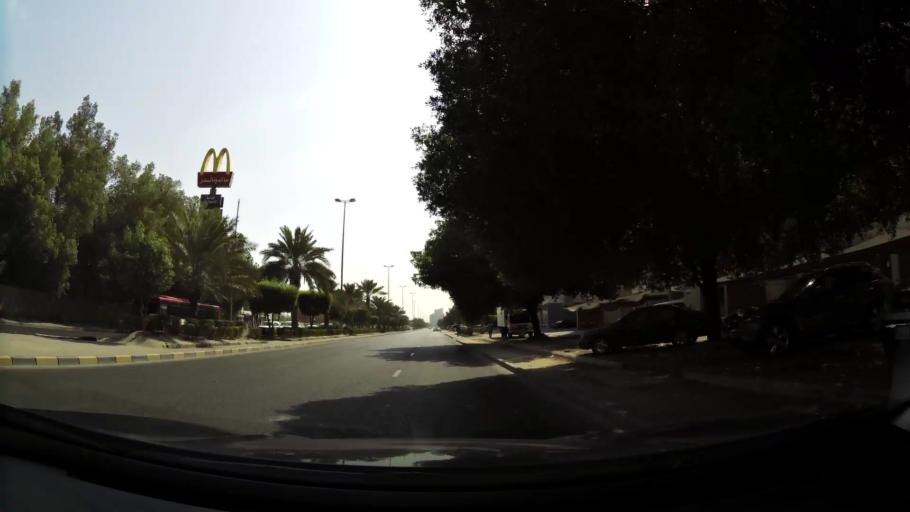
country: KW
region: Al Ahmadi
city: Al Mahbulah
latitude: 29.1441
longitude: 48.1286
